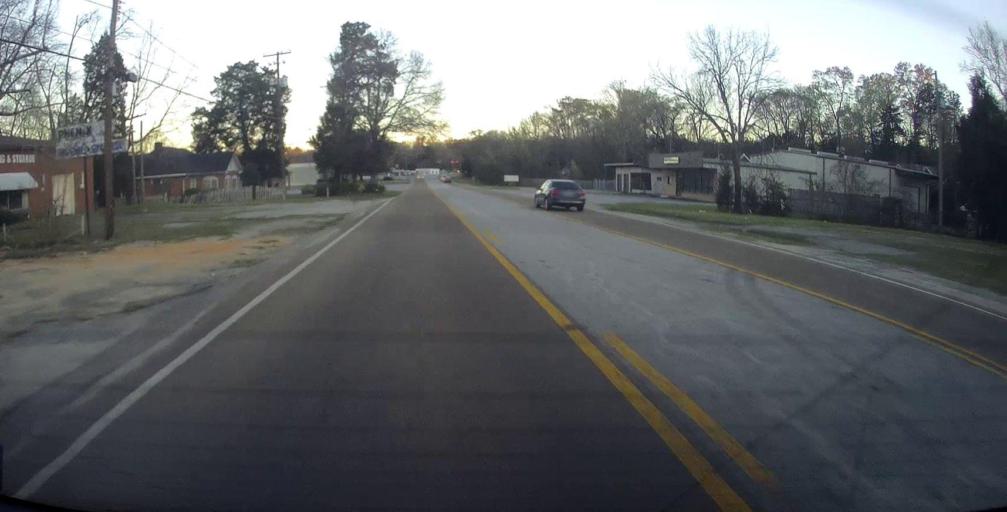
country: US
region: Alabama
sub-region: Russell County
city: Phenix City
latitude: 32.4773
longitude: -85.0258
